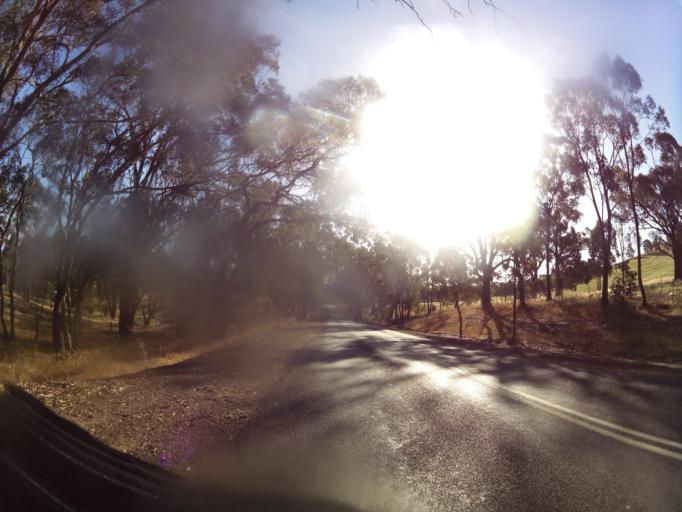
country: AU
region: Victoria
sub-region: Murrindindi
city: Kinglake West
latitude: -37.0108
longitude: 145.1214
